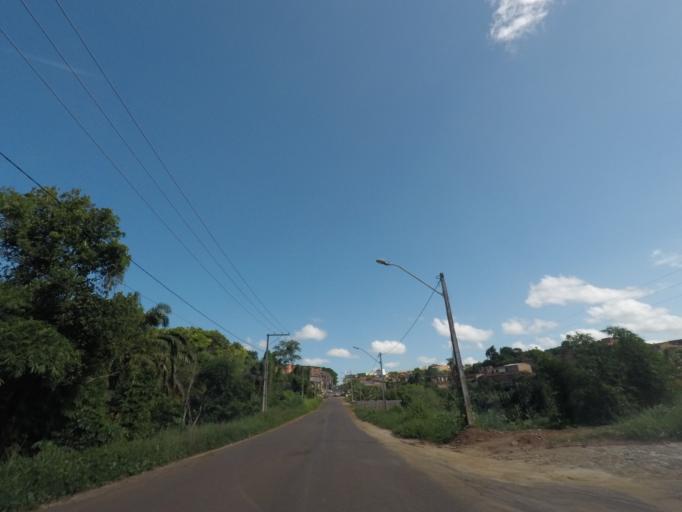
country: BR
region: Bahia
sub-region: Camamu
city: Camamu
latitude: -13.9377
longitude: -39.1068
